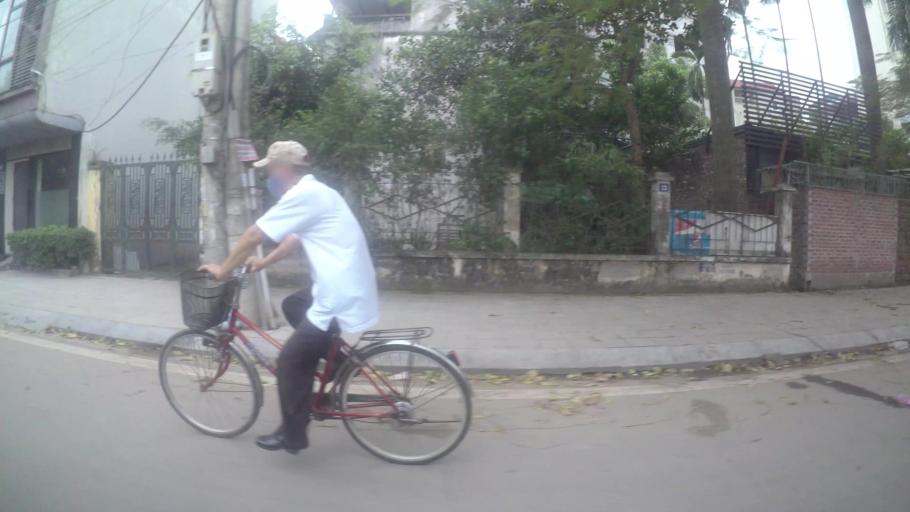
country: VN
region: Ha Noi
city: Tay Ho
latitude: 21.0563
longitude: 105.8209
